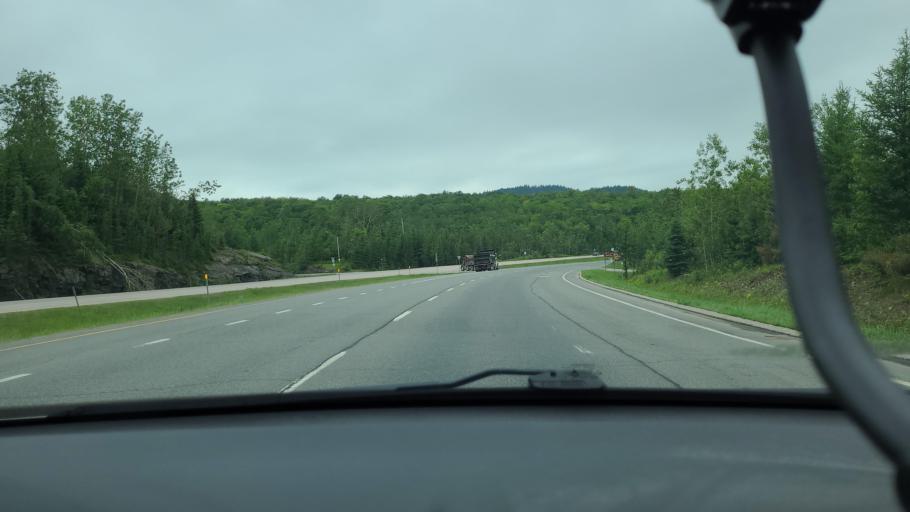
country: CA
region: Quebec
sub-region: Laurentides
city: Mont-Tremblant
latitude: 46.1394
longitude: -74.6436
